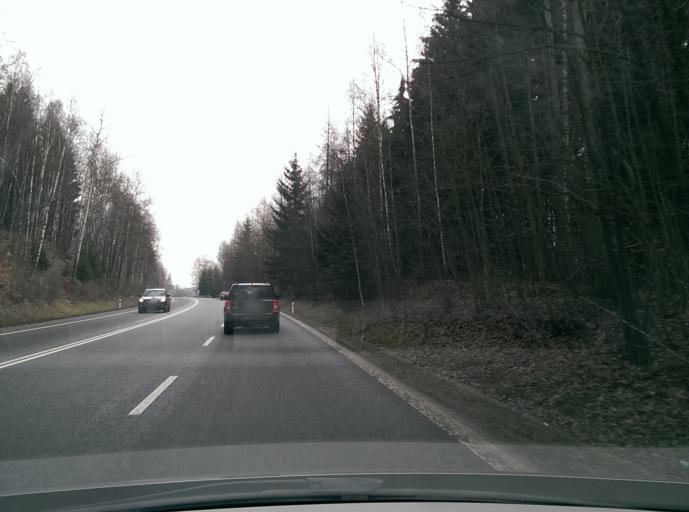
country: CZ
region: Liberecky
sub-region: Okres Jablonec nad Nisou
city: Jablonec nad Nisou
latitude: 50.6898
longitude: 15.1382
